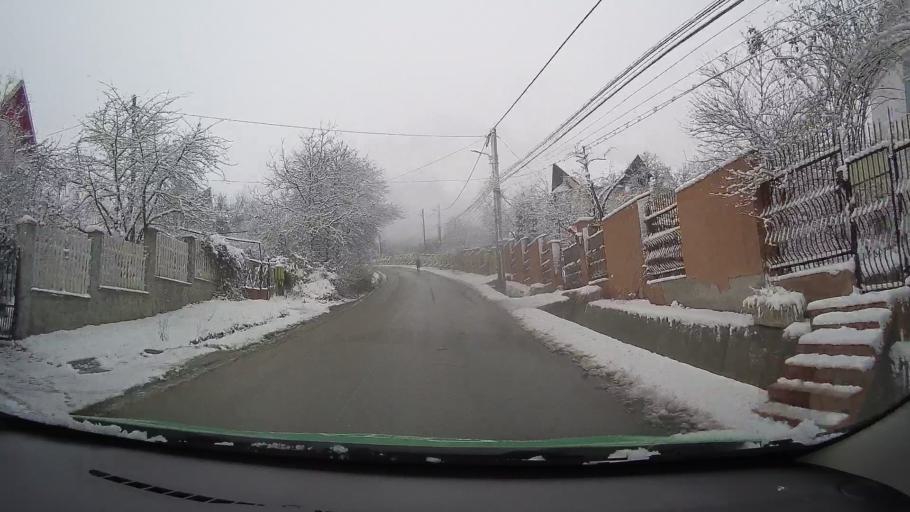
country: RO
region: Hunedoara
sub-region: Municipiul Deva
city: Deva
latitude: 45.8697
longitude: 22.8927
